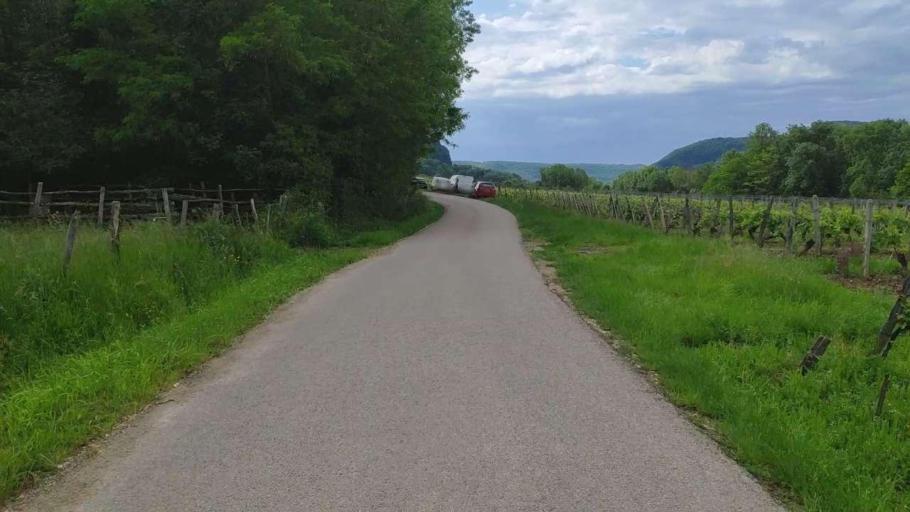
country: FR
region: Franche-Comte
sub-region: Departement du Jura
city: Perrigny
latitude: 46.7643
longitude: 5.6097
